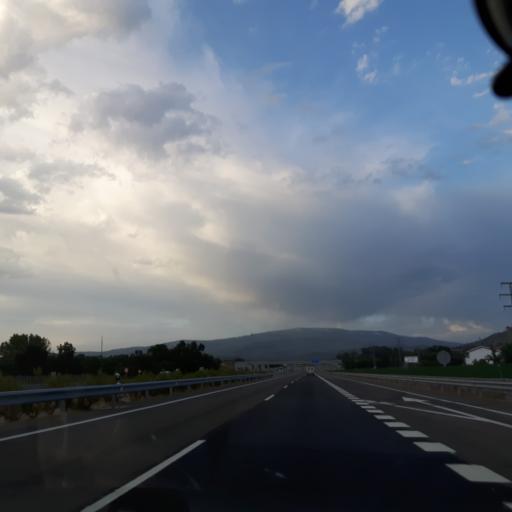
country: ES
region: Castille and Leon
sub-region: Provincia de Salamanca
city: Nava de Bejar
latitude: 40.4924
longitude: -5.6764
